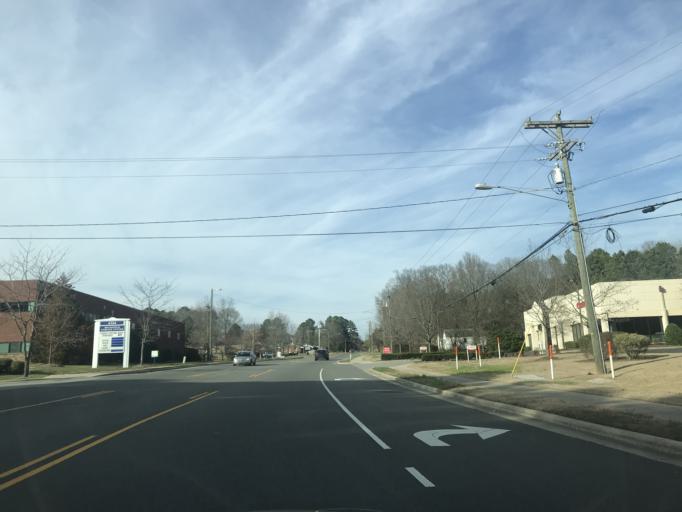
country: US
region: North Carolina
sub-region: Durham County
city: Durham
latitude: 35.9110
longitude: -78.8890
